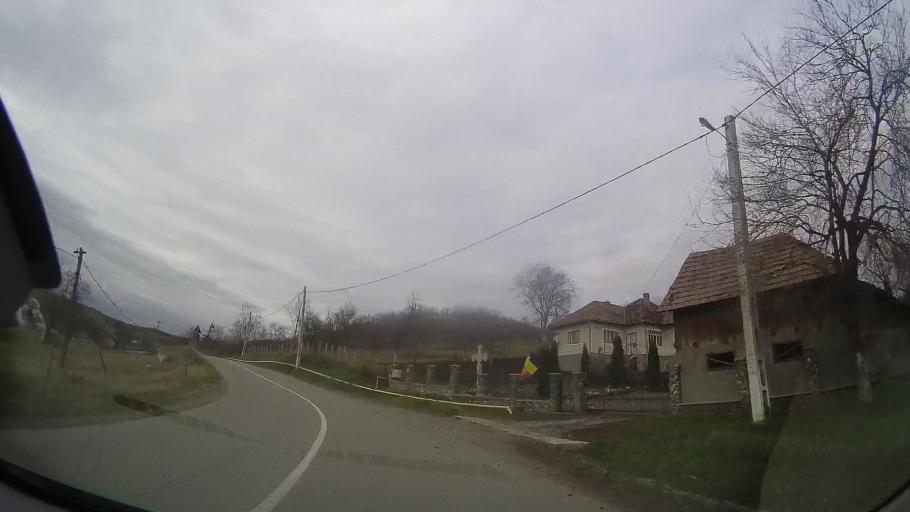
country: RO
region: Bistrita-Nasaud
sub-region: Comuna Milas
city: Milas
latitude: 46.8120
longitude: 24.4346
